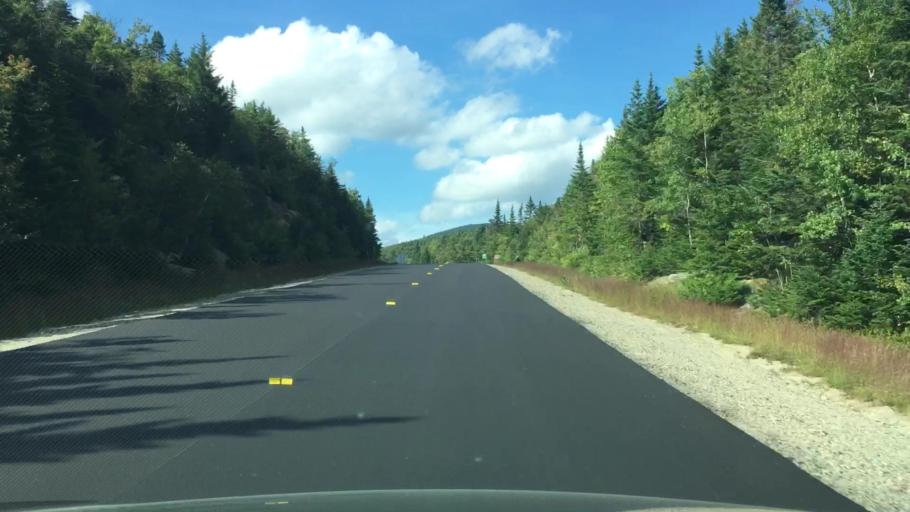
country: US
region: New Hampshire
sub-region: Grafton County
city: Woodstock
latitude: 44.0238
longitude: -71.4927
